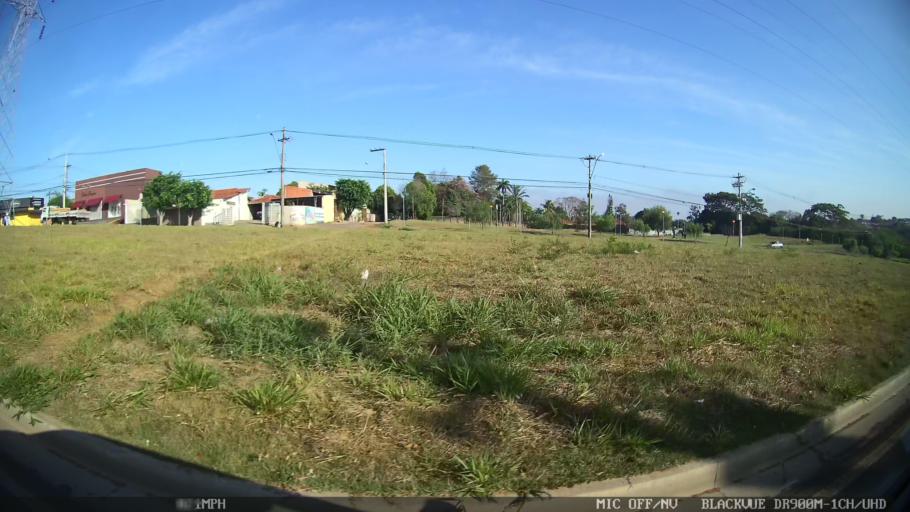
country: BR
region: Sao Paulo
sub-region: Sao Jose Do Rio Preto
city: Sao Jose do Rio Preto
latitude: -20.7864
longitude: -49.3435
